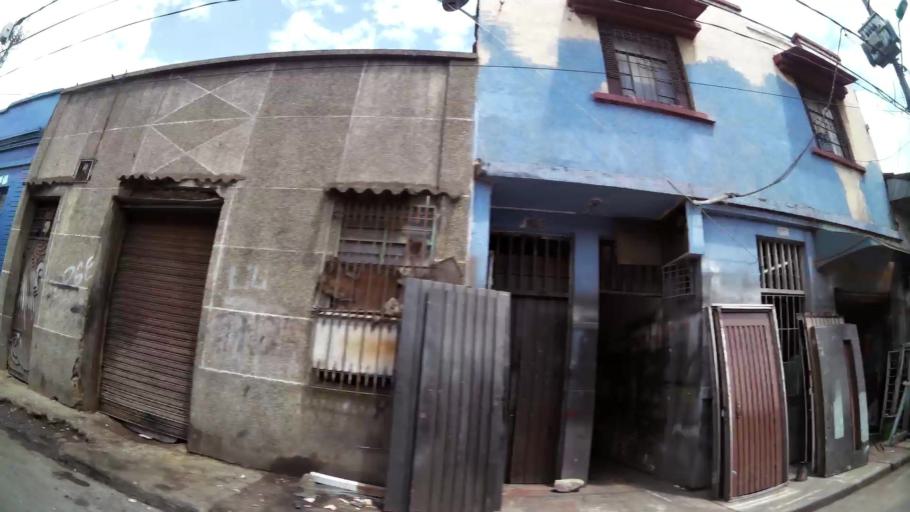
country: CO
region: Valle del Cauca
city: Cali
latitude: 3.4467
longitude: -76.5261
